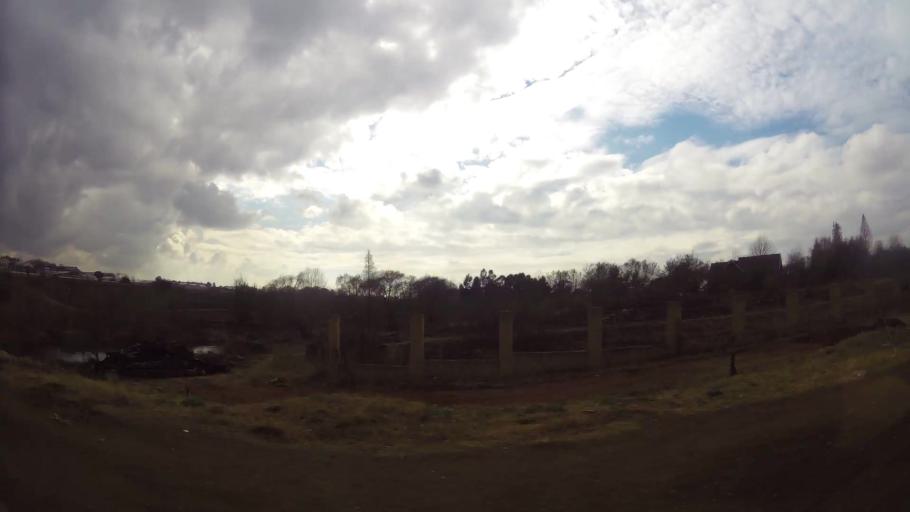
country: ZA
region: Gauteng
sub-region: Sedibeng District Municipality
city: Meyerton
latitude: -26.5835
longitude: 28.0165
